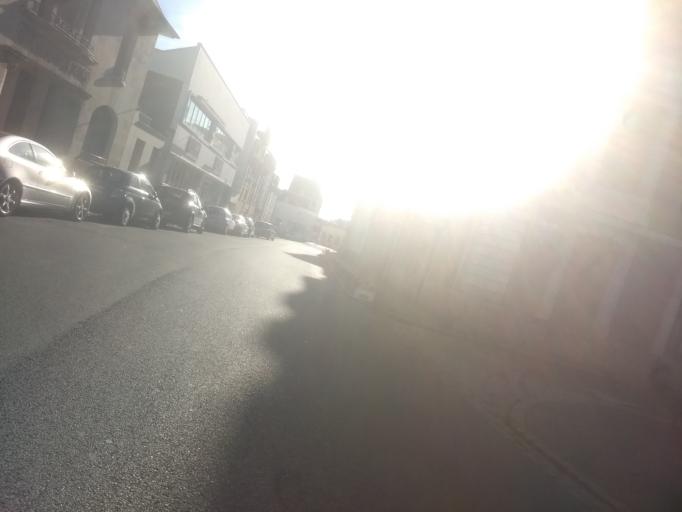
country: FR
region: Nord-Pas-de-Calais
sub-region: Departement du Pas-de-Calais
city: Arras
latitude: 50.2939
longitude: 2.7689
